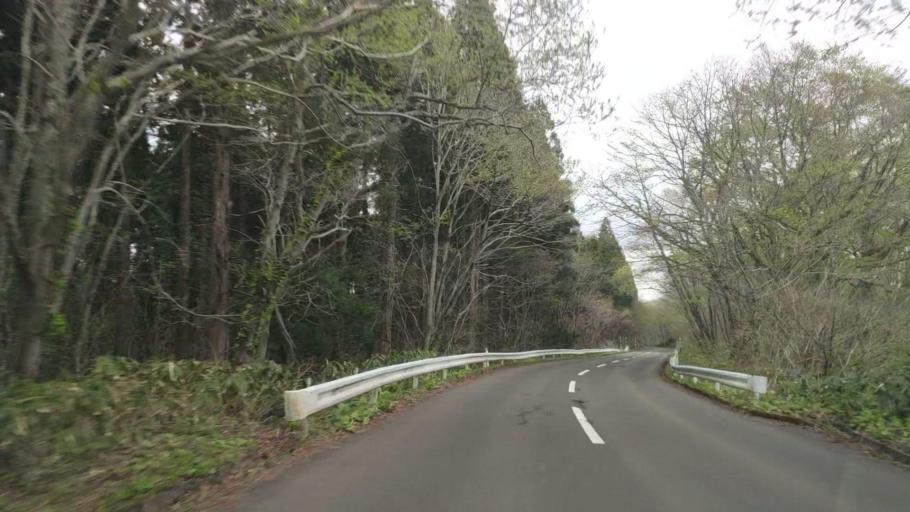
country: JP
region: Akita
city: Hanawa
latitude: 40.3904
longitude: 140.7950
